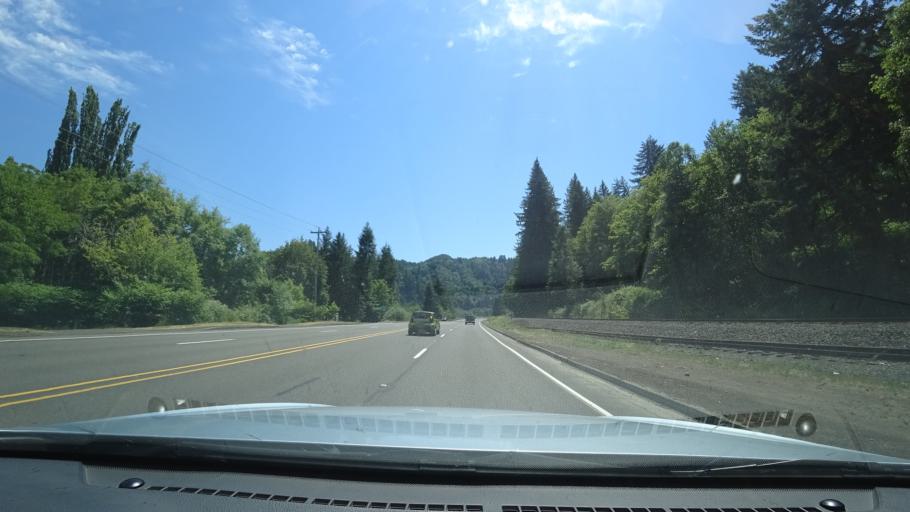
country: US
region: Oregon
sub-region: Lane County
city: Florence
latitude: 44.0236
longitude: -123.8581
